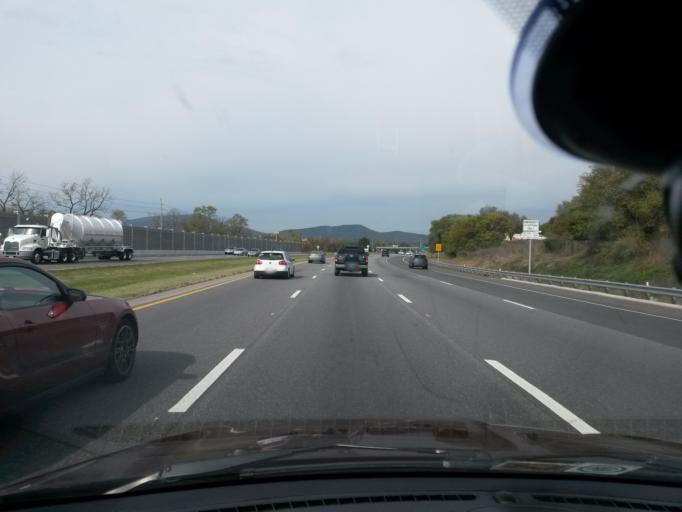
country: US
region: Virginia
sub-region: City of Roanoke
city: Roanoke
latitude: 37.3042
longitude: -79.9686
